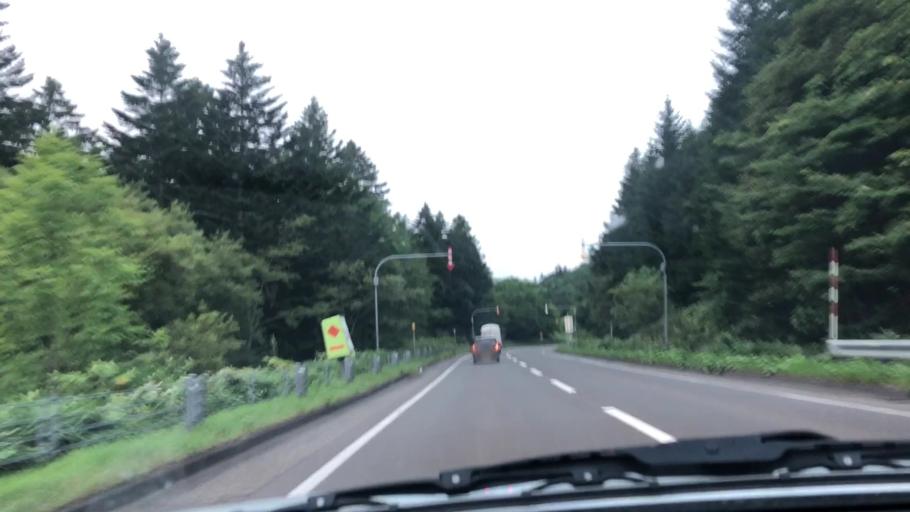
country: JP
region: Hokkaido
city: Iwamizawa
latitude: 42.9129
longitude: 142.1212
